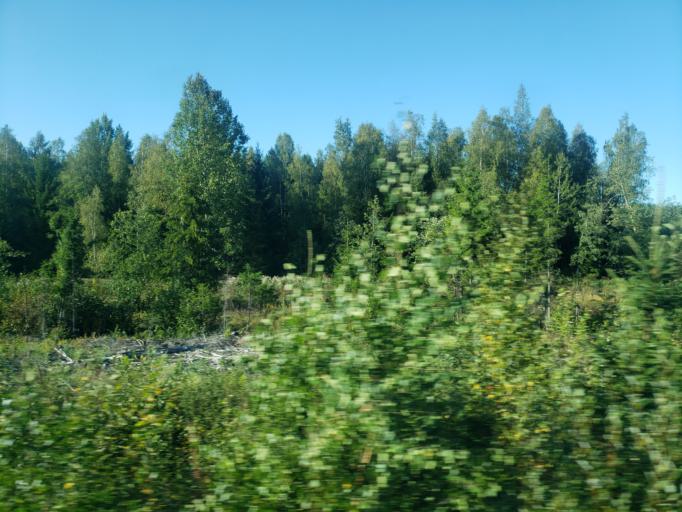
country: FI
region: South Karelia
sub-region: Lappeenranta
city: Ylaemaa
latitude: 60.9320
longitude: 27.9099
